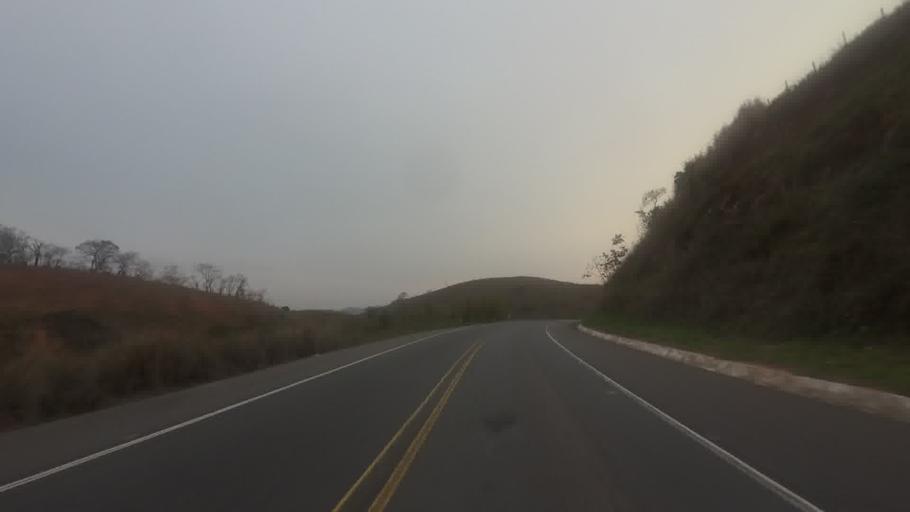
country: BR
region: Rio de Janeiro
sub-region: Carmo
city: Carmo
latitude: -21.7555
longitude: -42.4799
